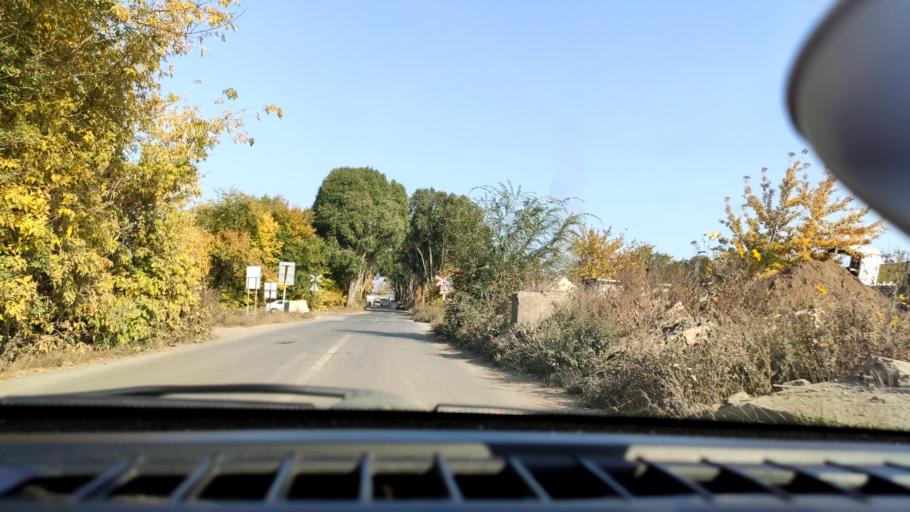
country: RU
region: Samara
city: Samara
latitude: 53.1922
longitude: 50.2708
